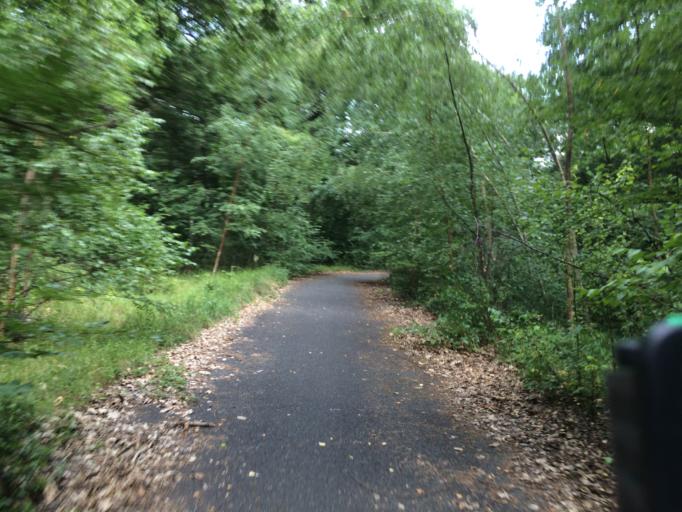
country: FR
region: Ile-de-France
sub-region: Departement de l'Essonne
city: Soisy-sur-Seine
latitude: 48.6640
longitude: 2.4455
